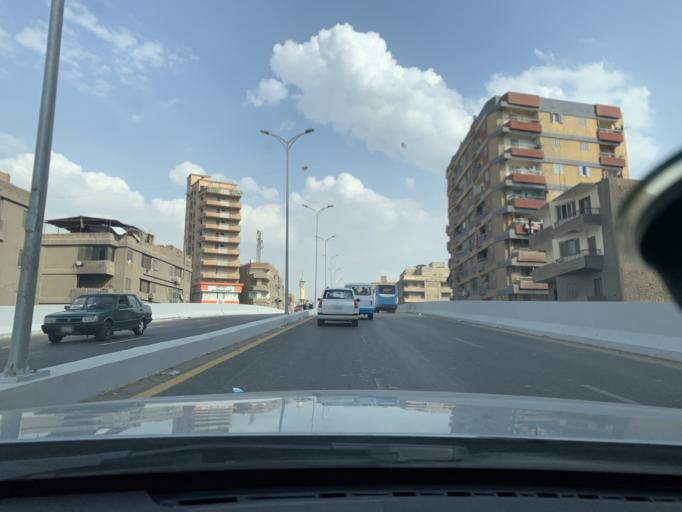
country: EG
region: Muhafazat al Qahirah
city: Cairo
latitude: 30.1269
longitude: 31.2974
